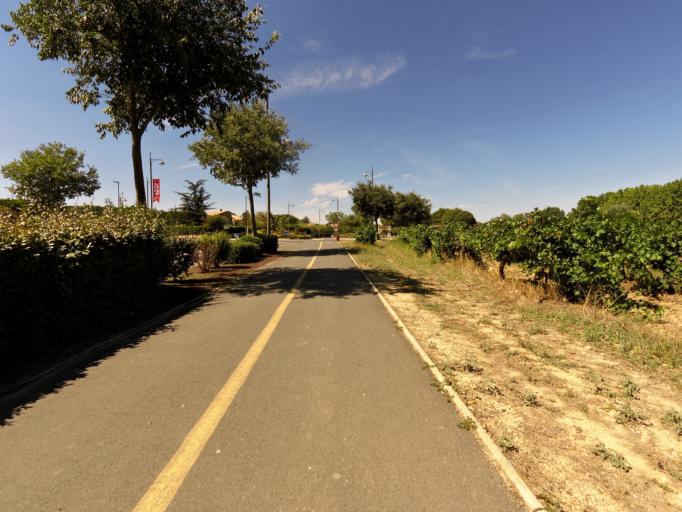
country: FR
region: Languedoc-Roussillon
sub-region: Departement du Gard
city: Sommieres
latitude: 43.7850
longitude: 4.0851
